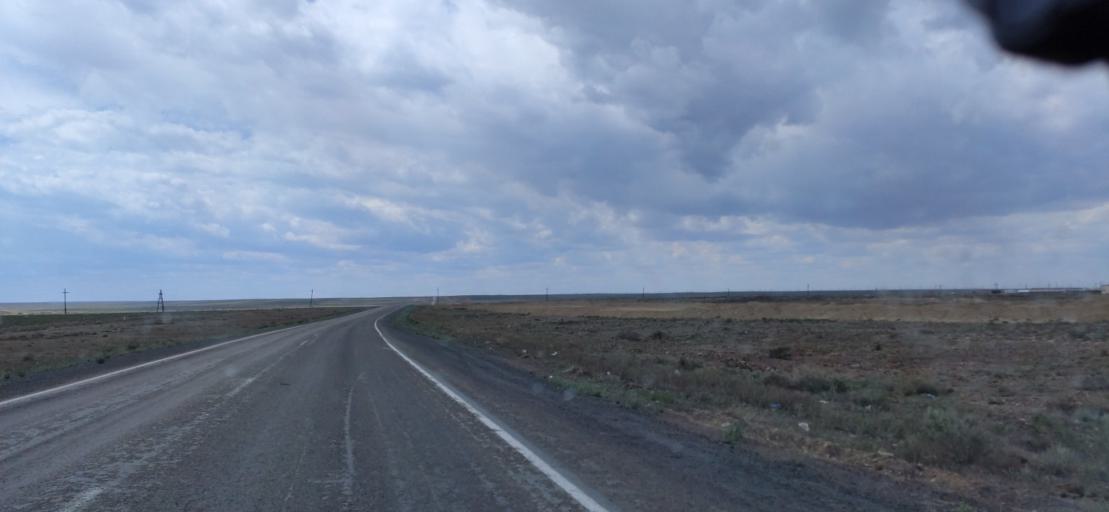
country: KZ
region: Qaraghandy
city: Saryshaghan
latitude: 46.0100
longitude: 73.5886
